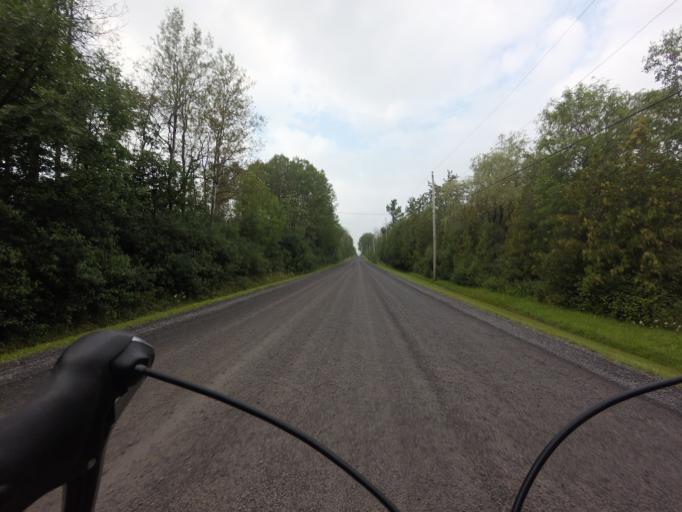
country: CA
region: Ontario
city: Bells Corners
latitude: 45.1103
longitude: -75.7899
